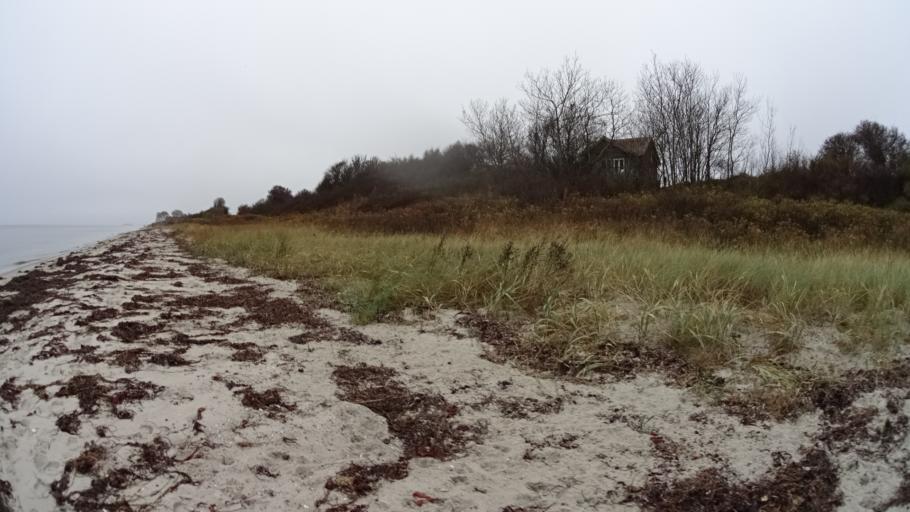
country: DK
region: Central Jutland
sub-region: Odder Kommune
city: Odder
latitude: 55.9429
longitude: 10.2605
